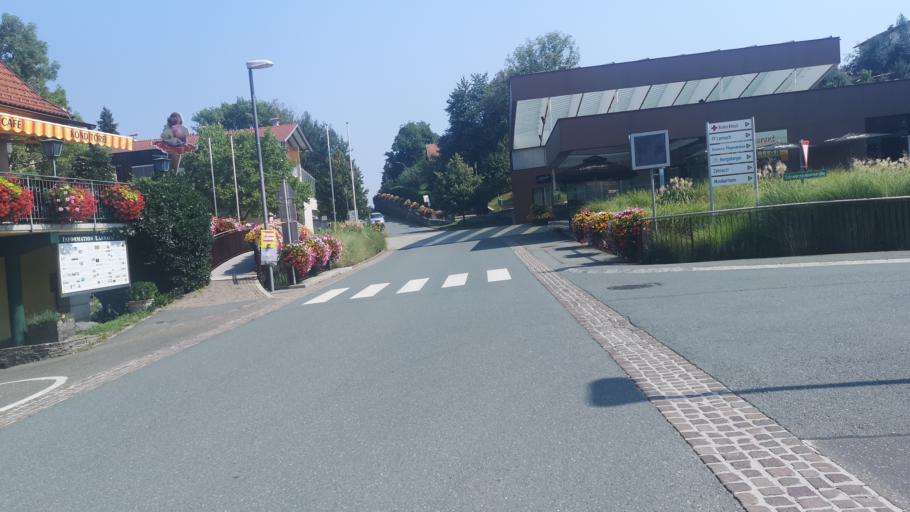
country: AT
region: Styria
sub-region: Politischer Bezirk Deutschlandsberg
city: Lannach
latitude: 46.9431
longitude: 15.3330
